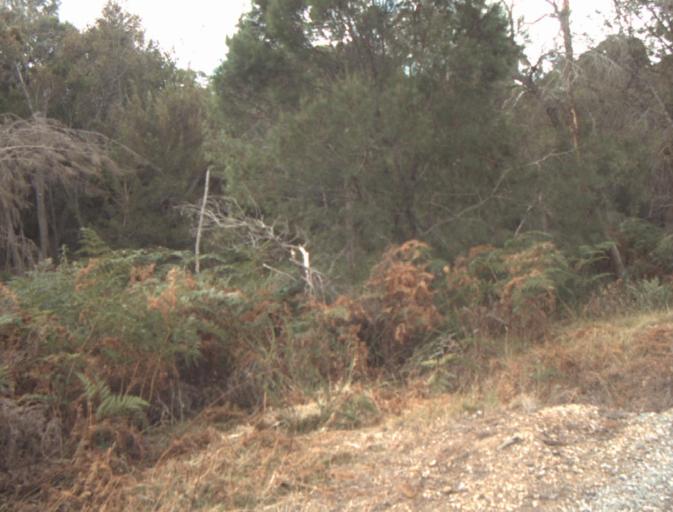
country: AU
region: Tasmania
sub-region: Launceston
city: Mayfield
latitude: -41.2830
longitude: 147.0165
